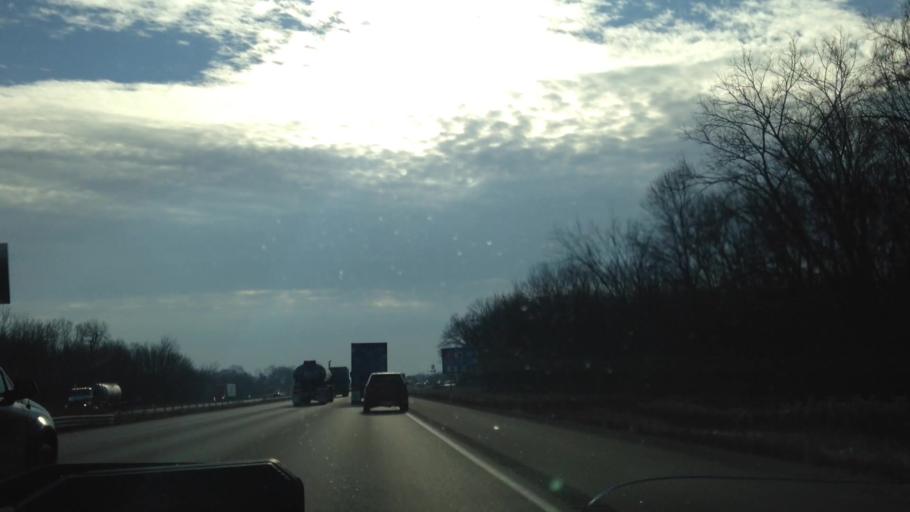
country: US
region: Wisconsin
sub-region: Waukesha County
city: Menomonee Falls
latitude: 43.2018
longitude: -88.1340
